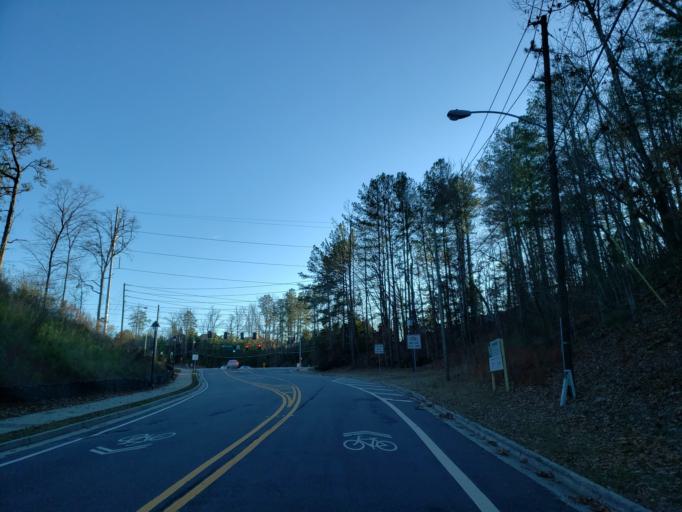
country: US
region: Georgia
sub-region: Fulton County
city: Sandy Springs
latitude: 33.9375
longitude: -84.3665
